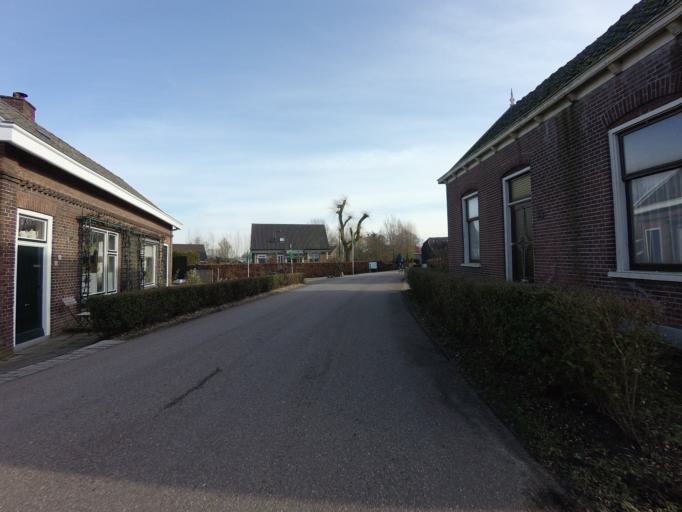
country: NL
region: South Holland
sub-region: Gemeente Hardinxveld-Giessendam
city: Neder-Hardinxveld
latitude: 51.8335
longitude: 4.8523
